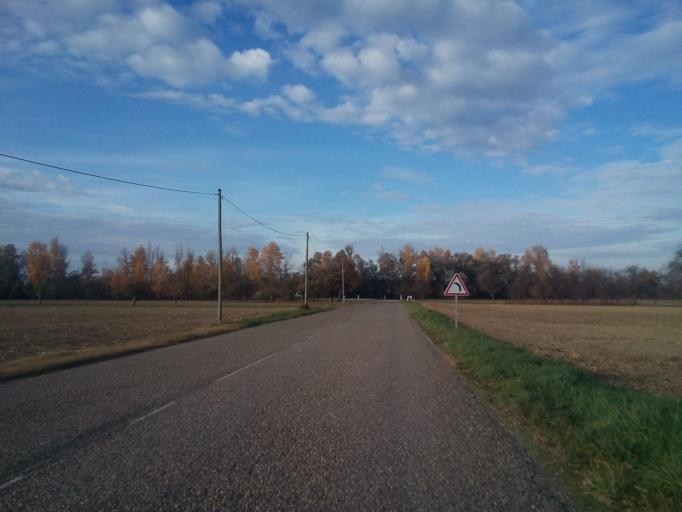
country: FR
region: Alsace
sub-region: Departement du Bas-Rhin
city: Herrlisheim
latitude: 48.7012
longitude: 7.9207
